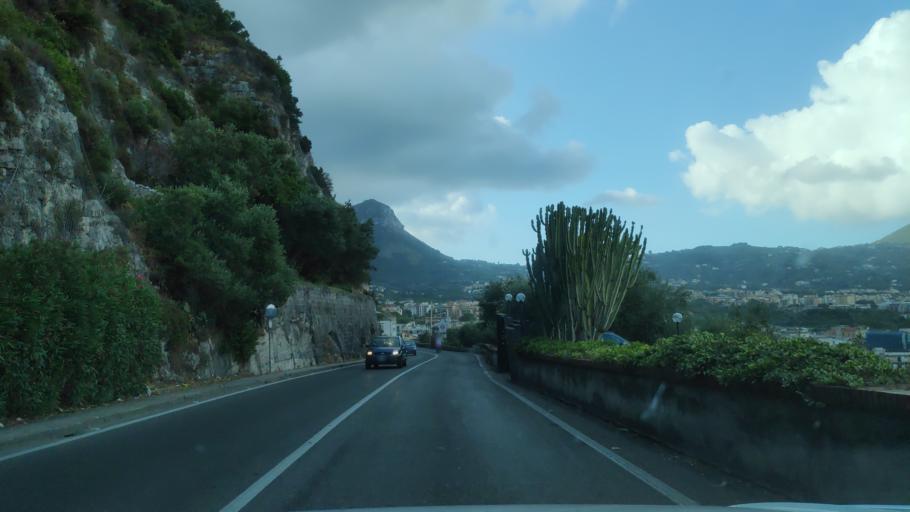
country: IT
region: Campania
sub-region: Provincia di Napoli
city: Meta
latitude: 40.6463
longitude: 14.4133
